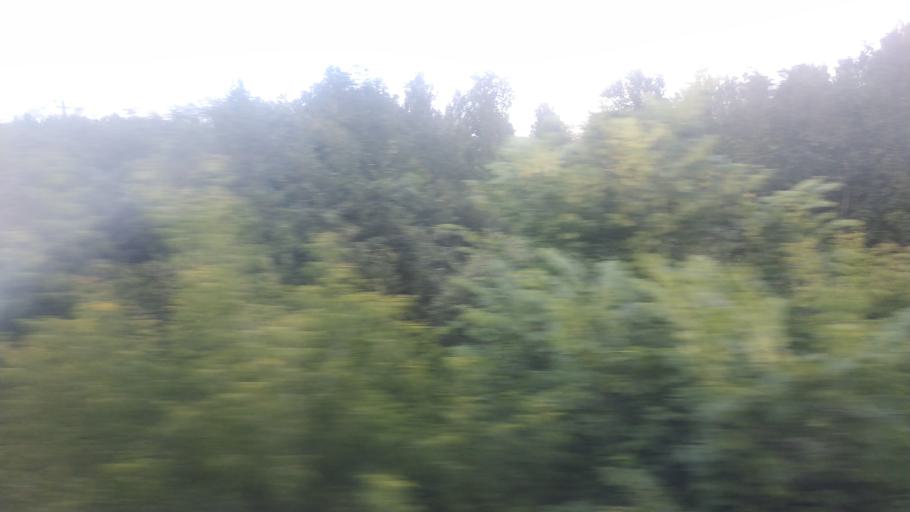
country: RU
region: Moskovskaya
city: Tugolesskiy Bor
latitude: 55.5588
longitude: 39.7013
